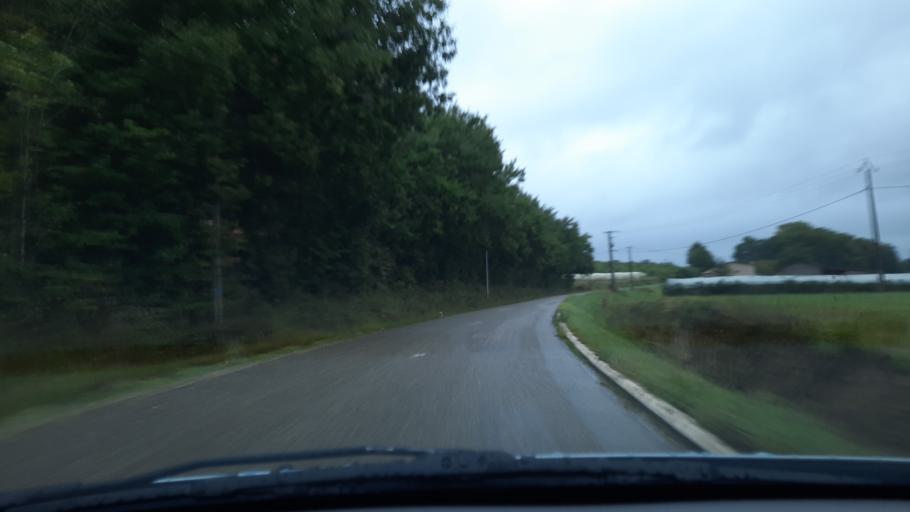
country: FR
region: Midi-Pyrenees
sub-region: Departement du Tarn-et-Garonne
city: Lafrancaise
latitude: 44.1836
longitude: 1.2728
